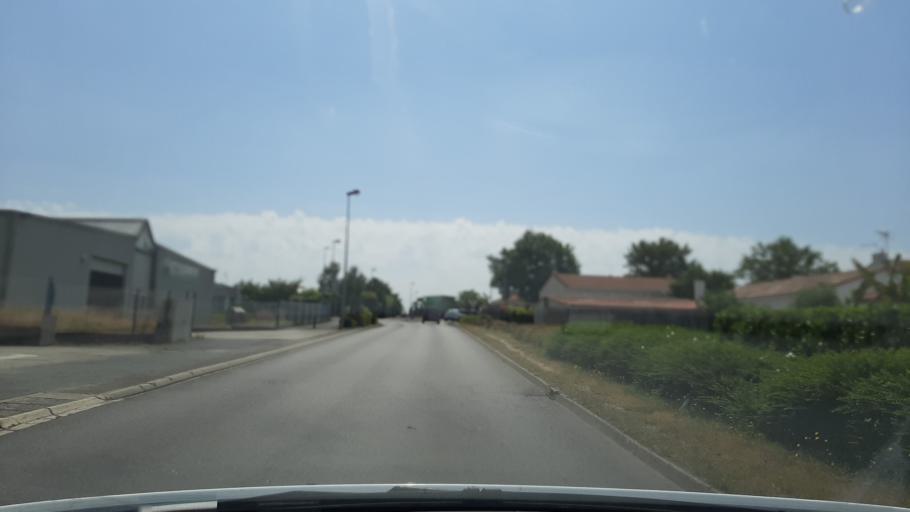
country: FR
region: Pays de la Loire
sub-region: Departement de la Vendee
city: Le Poire-sur-Vie
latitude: 46.7679
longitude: -1.5014
